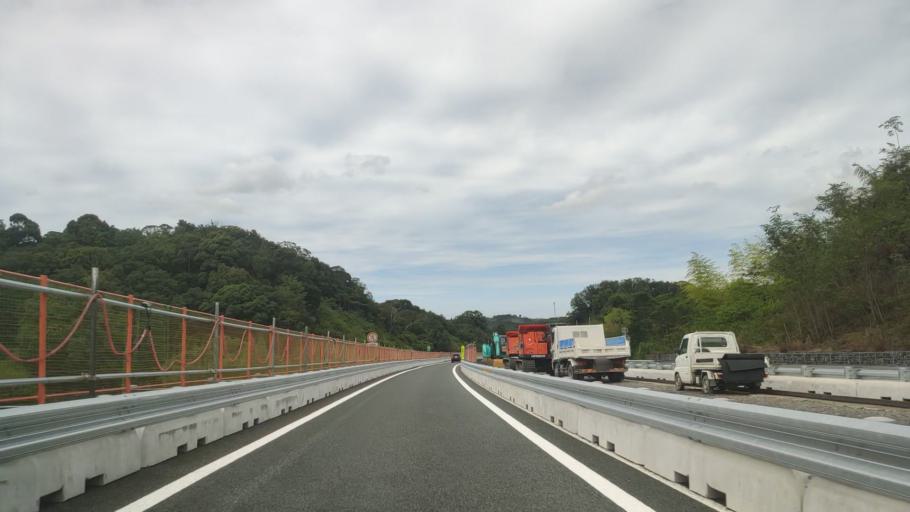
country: JP
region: Wakayama
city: Gobo
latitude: 33.8640
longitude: 135.1928
